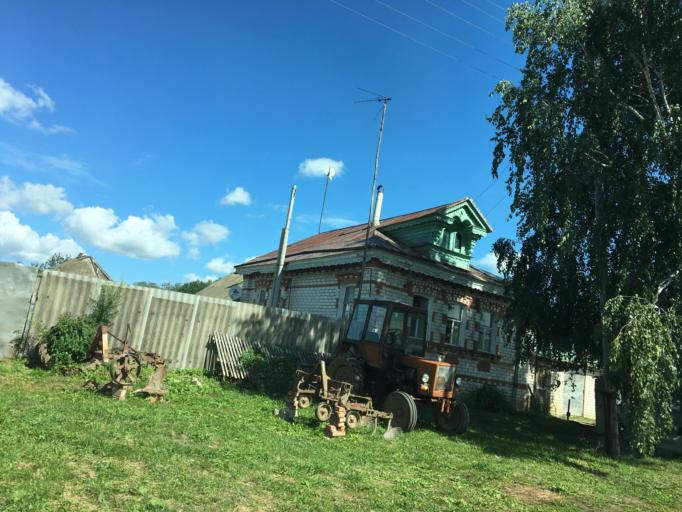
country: RU
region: Nizjnij Novgorod
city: Lyskovo
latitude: 55.9844
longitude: 45.0357
